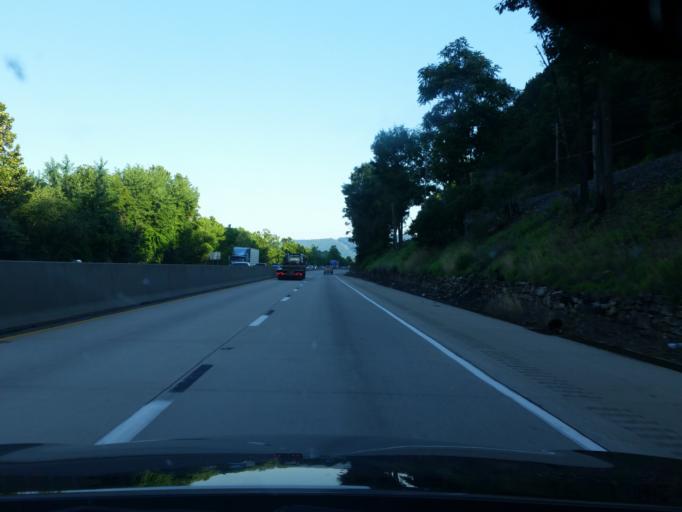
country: US
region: Pennsylvania
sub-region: Perry County
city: Marysville
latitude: 40.3531
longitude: -76.9181
